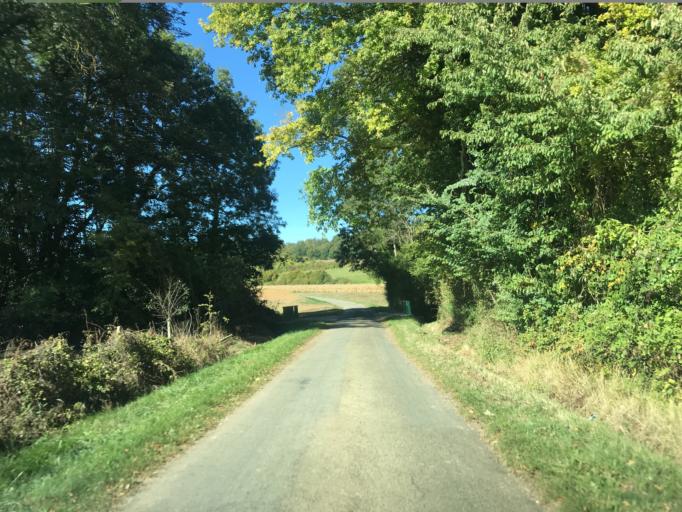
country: FR
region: Haute-Normandie
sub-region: Departement de l'Eure
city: Saint-Aubin-sur-Gaillon
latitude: 49.1719
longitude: 1.2731
